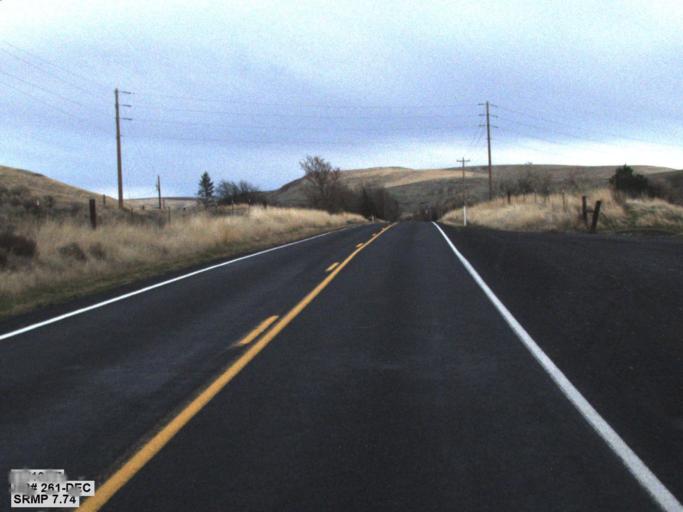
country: US
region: Washington
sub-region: Columbia County
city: Dayton
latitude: 46.5189
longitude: -118.1217
